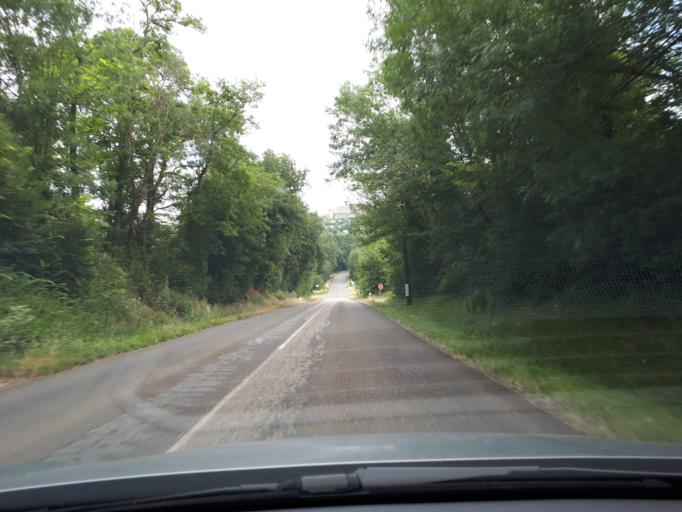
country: FR
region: Midi-Pyrenees
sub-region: Departement du Gers
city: Lectoure
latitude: 43.9343
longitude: 0.6016
